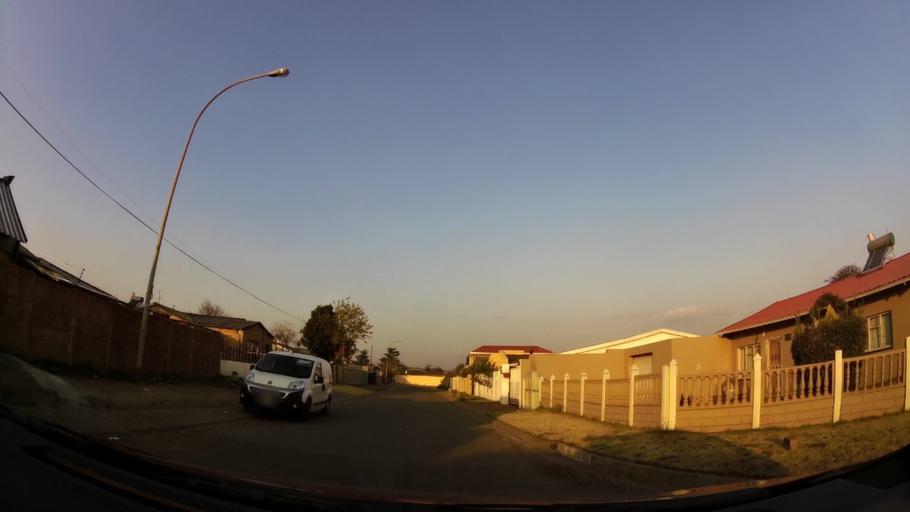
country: ZA
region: Gauteng
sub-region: City of Johannesburg Metropolitan Municipality
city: Soweto
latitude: -26.2817
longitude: 27.9041
